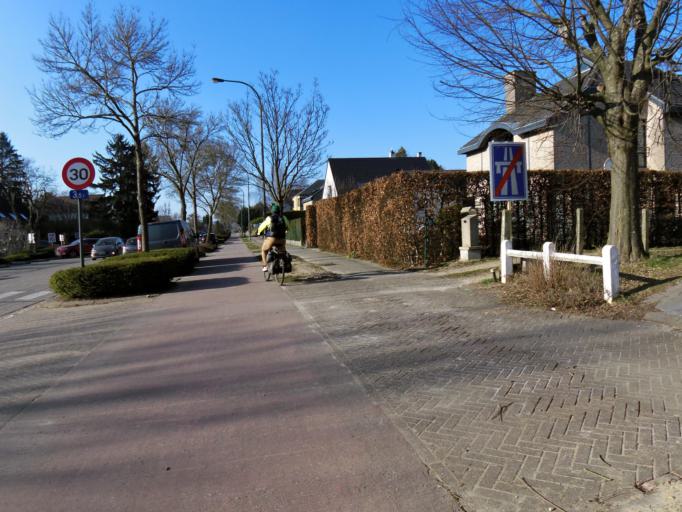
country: BE
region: Flanders
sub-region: Provincie Vlaams-Brabant
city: Wezembeek-Oppem
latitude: 50.8480
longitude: 4.5073
